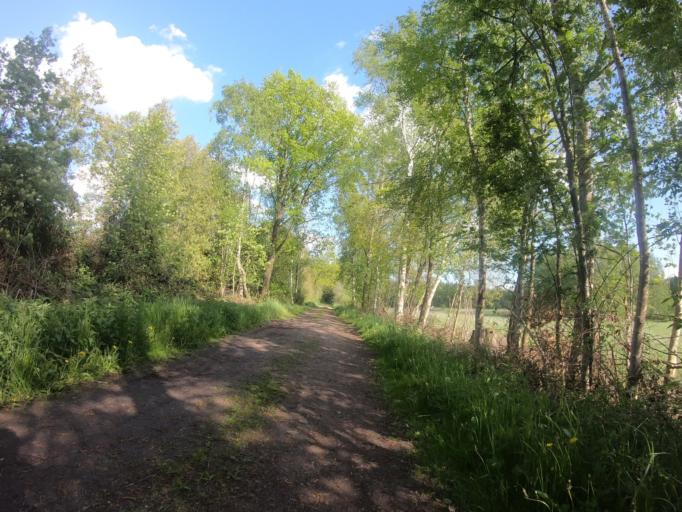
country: DE
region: Lower Saxony
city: Sassenburg
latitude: 52.5299
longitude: 10.6170
